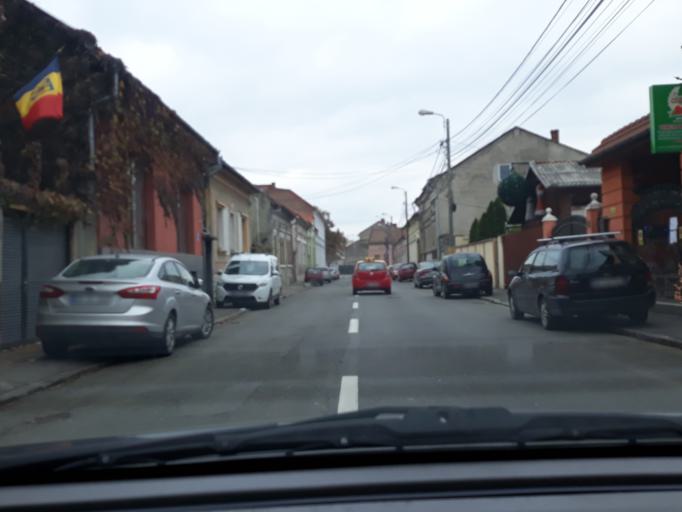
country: RO
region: Bihor
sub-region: Comuna Biharea
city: Oradea
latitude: 47.0623
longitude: 21.9267
